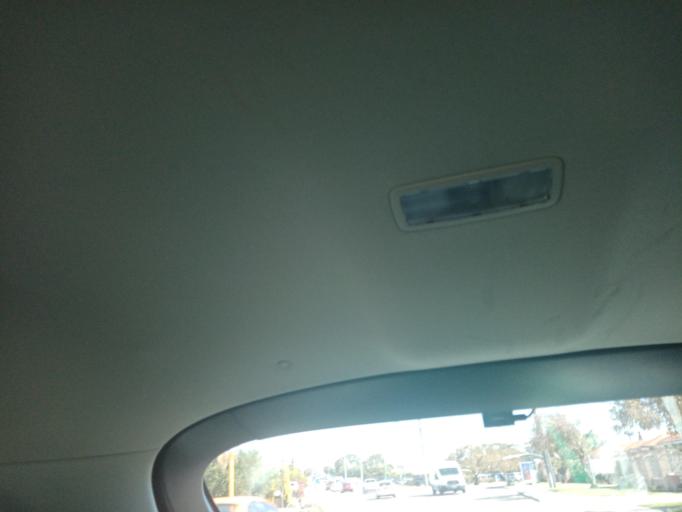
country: AU
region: Western Australia
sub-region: City of Cockburn
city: Spearwood
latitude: -32.1194
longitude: 115.7827
